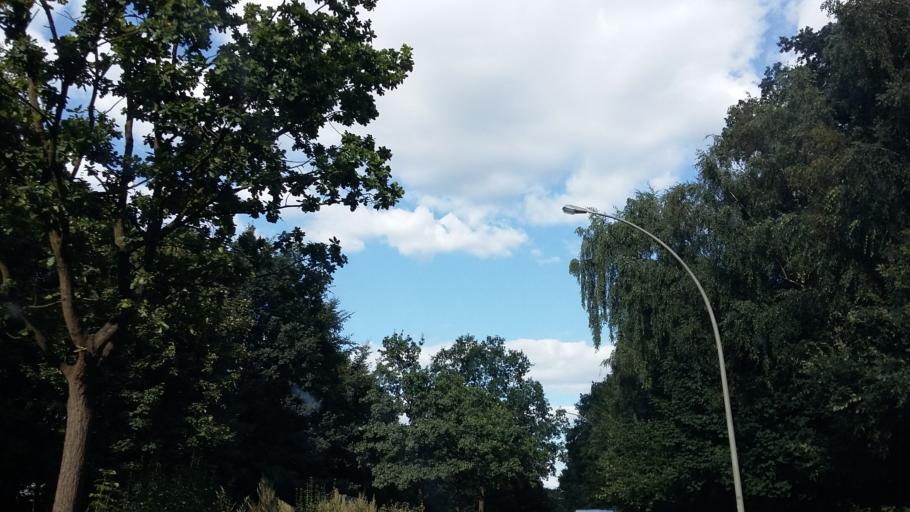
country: DE
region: Schleswig-Holstein
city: Halstenbek
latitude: 53.5705
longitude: 9.8318
